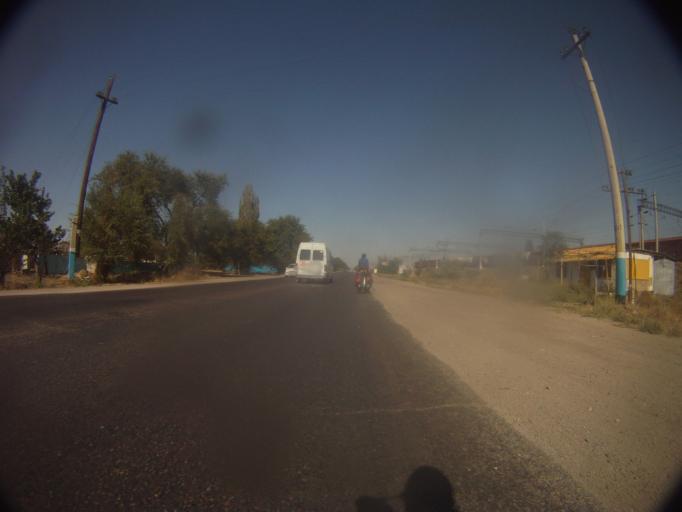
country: KZ
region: Zhambyl
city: Taraz
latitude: 42.9225
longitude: 71.4084
